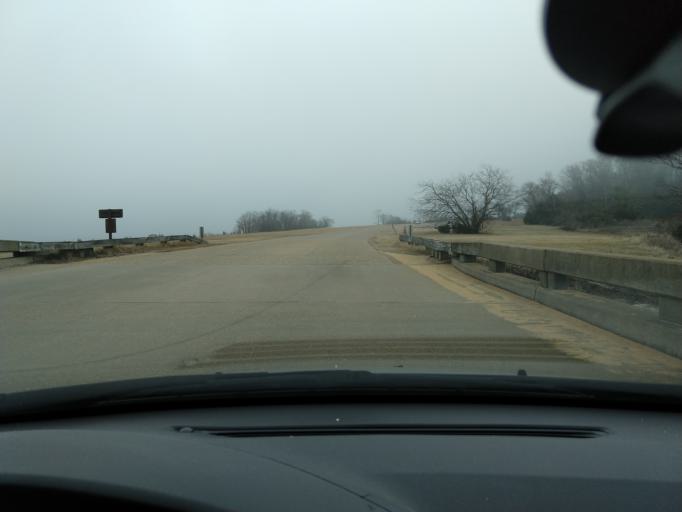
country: US
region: Virginia
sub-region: York County
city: Yorktown
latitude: 37.2689
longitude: -76.5570
